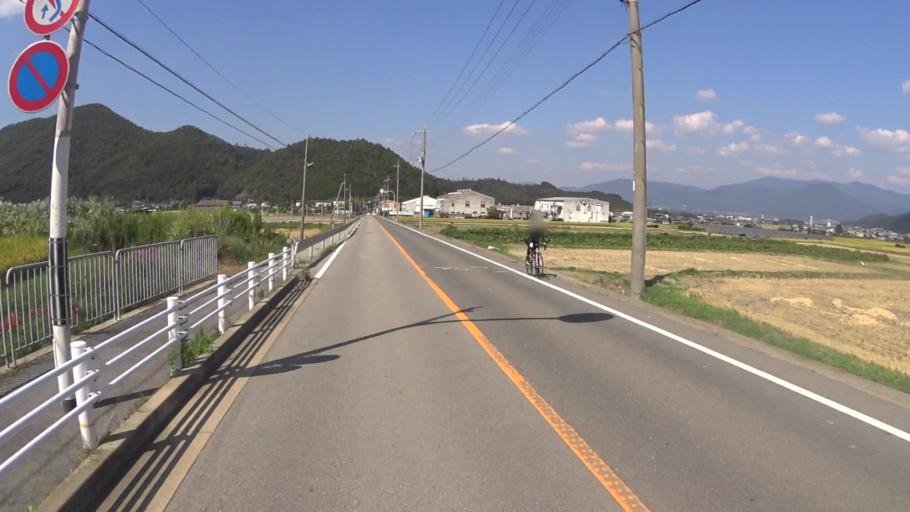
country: JP
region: Kyoto
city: Kameoka
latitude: 34.9896
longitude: 135.5364
